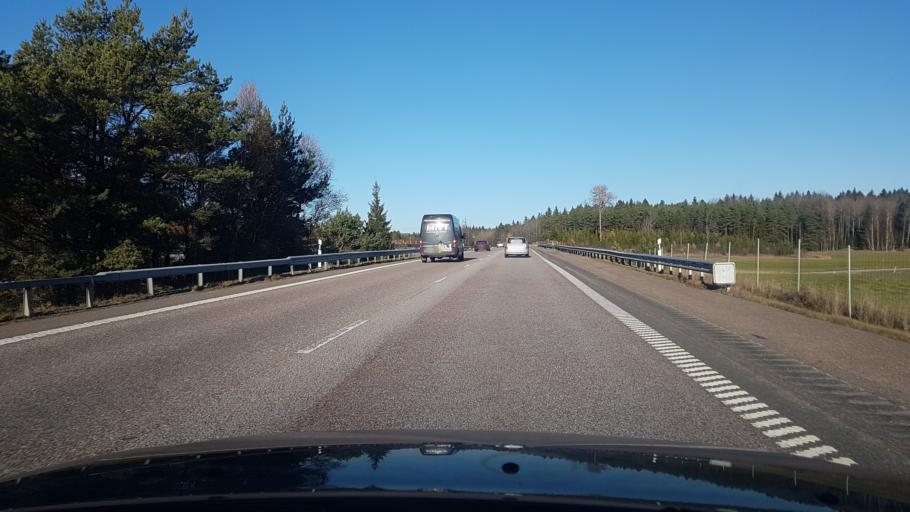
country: SE
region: Stockholm
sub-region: Sigtuna Kommun
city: Marsta
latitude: 59.6835
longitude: 17.8693
